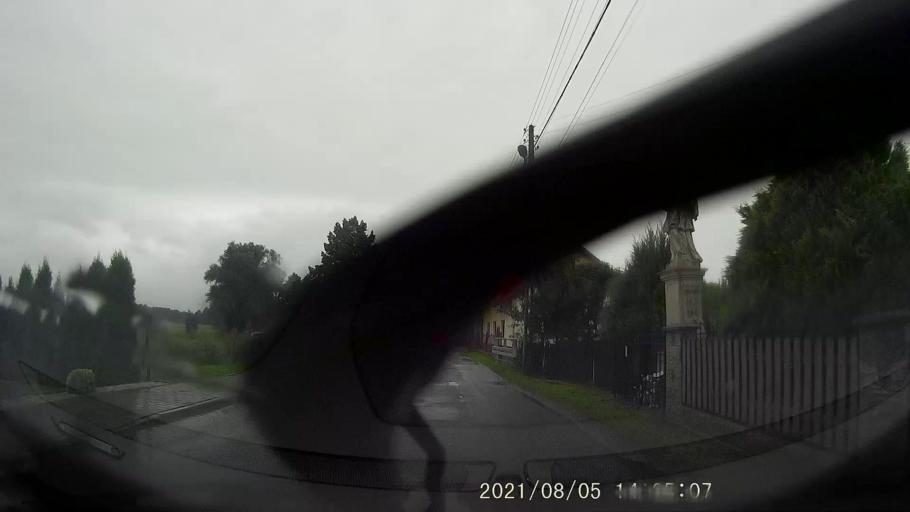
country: PL
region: Opole Voivodeship
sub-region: Powiat krapkowicki
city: Strzeleczki
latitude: 50.4629
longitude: 17.8554
